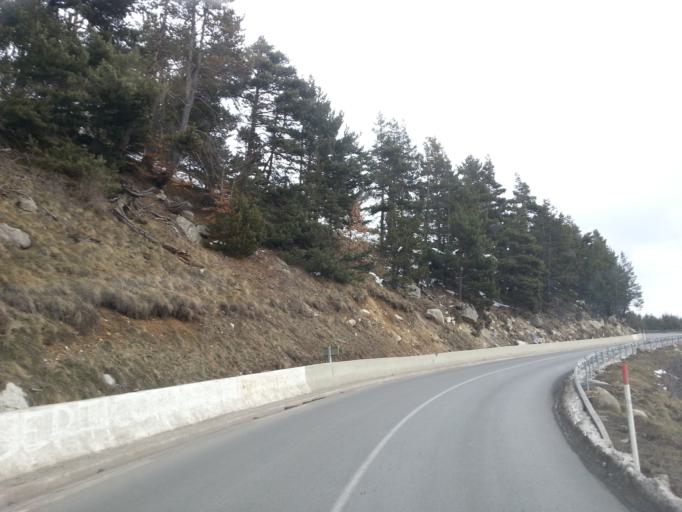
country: ES
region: Catalonia
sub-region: Provincia de Girona
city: Llivia
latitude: 42.5150
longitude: 2.1108
